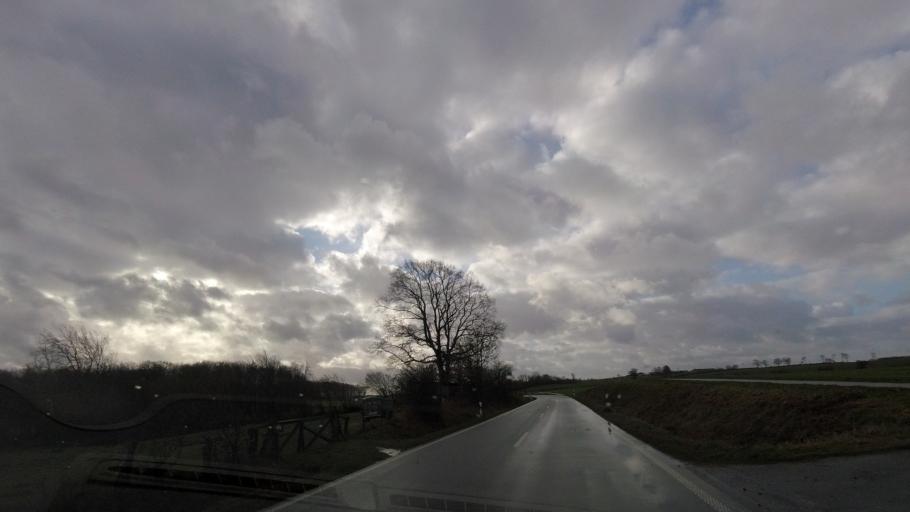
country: DE
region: Schleswig-Holstein
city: Kappeln
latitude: 54.6569
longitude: 9.9125
